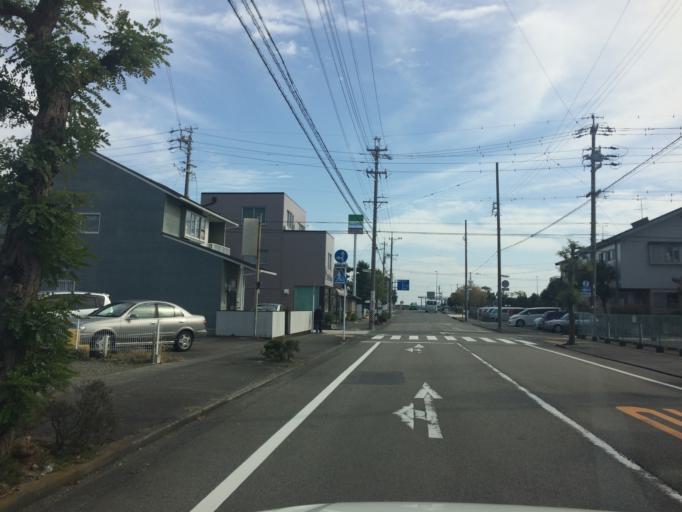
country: JP
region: Shizuoka
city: Yaizu
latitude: 34.8677
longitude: 138.3237
